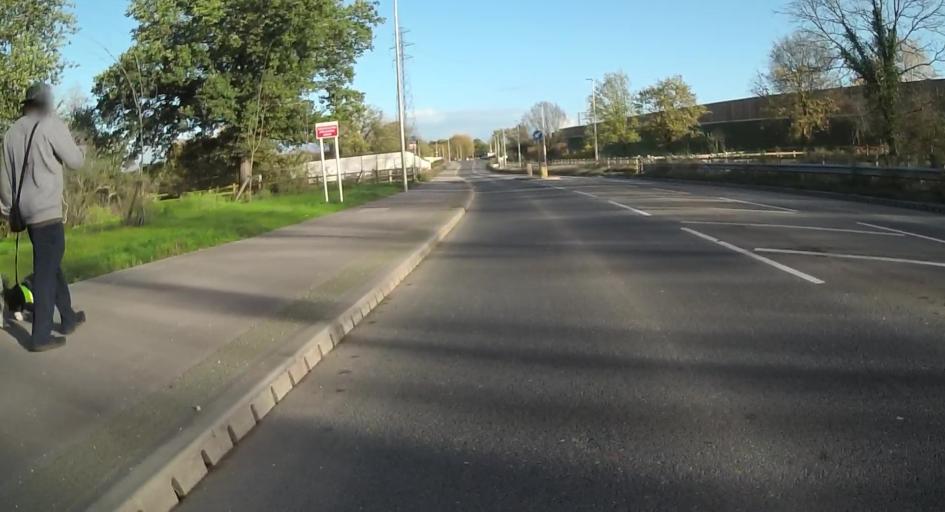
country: GB
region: England
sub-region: Wokingham
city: Winnersh
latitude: 51.4254
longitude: -0.8859
